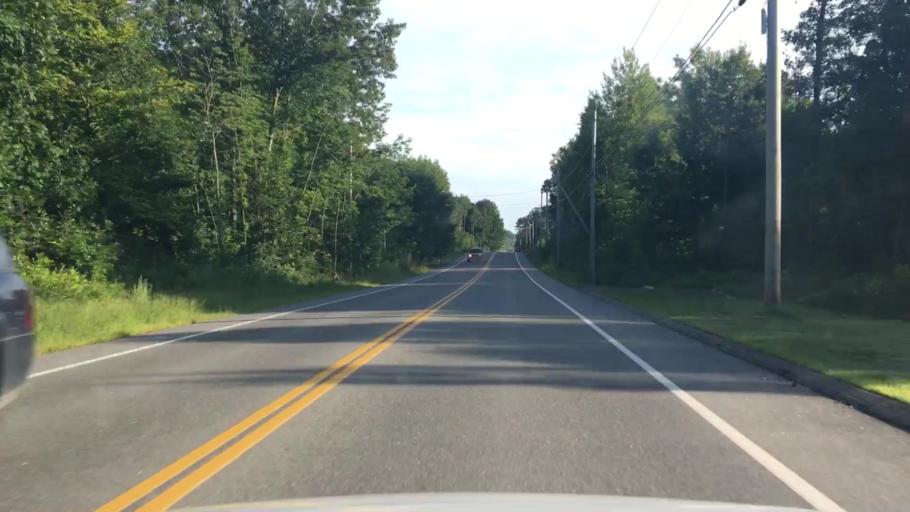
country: US
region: Maine
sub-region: Cumberland County
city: North Windham
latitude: 43.8104
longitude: -70.4410
